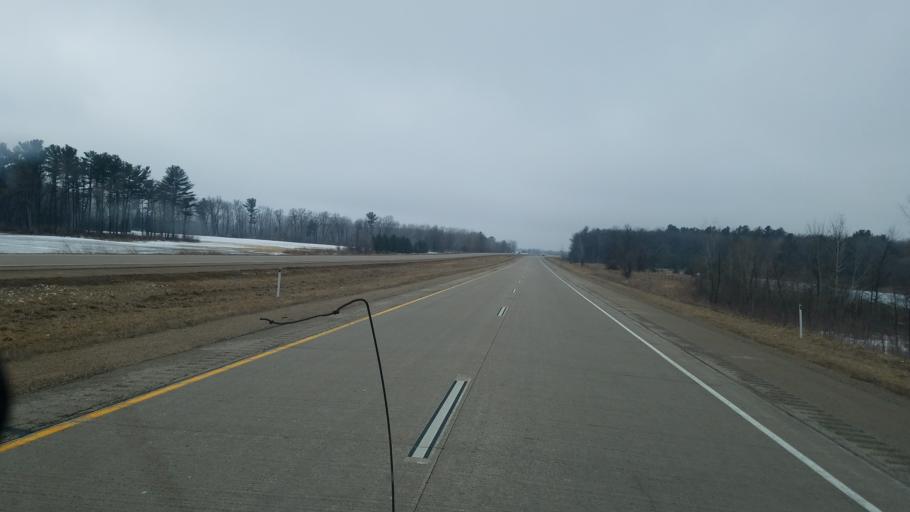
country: US
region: Wisconsin
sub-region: Waupaca County
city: Weyauwega
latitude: 44.2513
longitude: -88.8240
